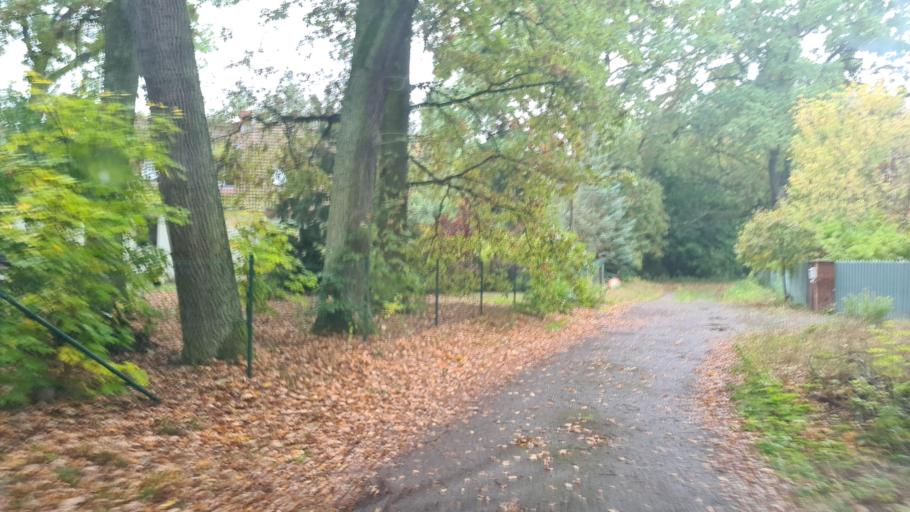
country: DE
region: Brandenburg
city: Storkow
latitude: 52.2228
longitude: 13.9349
